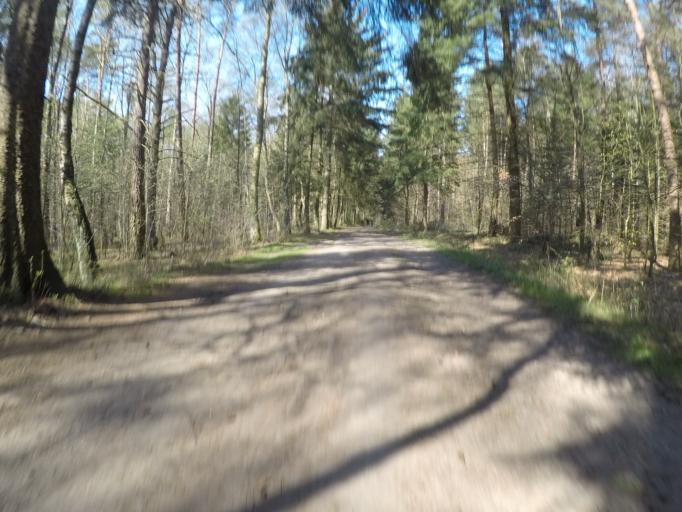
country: DE
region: Schleswig-Holstein
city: Appen
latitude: 53.6205
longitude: 9.7711
